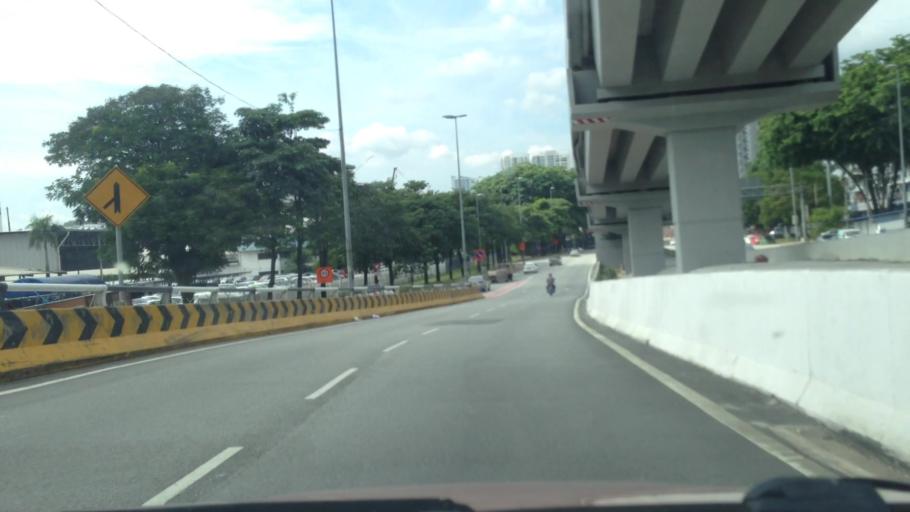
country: MY
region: Kuala Lumpur
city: Kuala Lumpur
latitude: 3.0914
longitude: 101.6916
